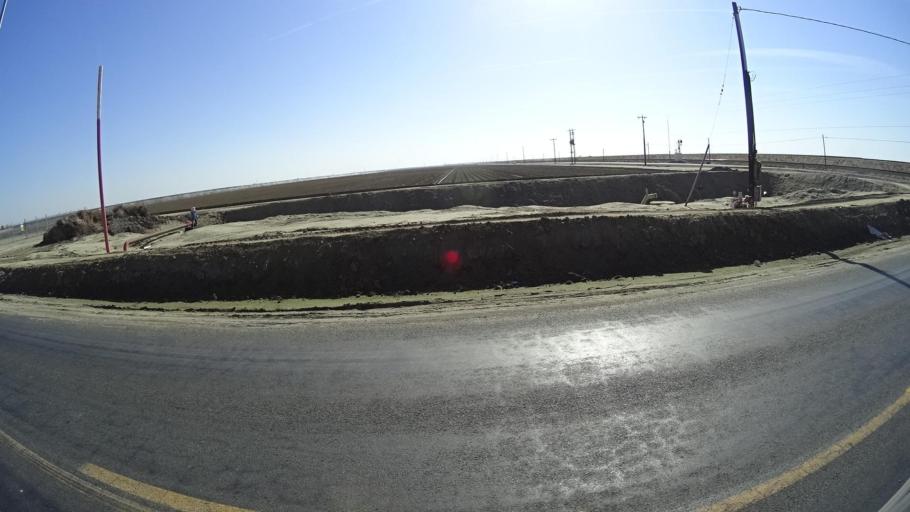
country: US
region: California
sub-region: Kern County
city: Wasco
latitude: 35.6449
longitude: -119.3301
